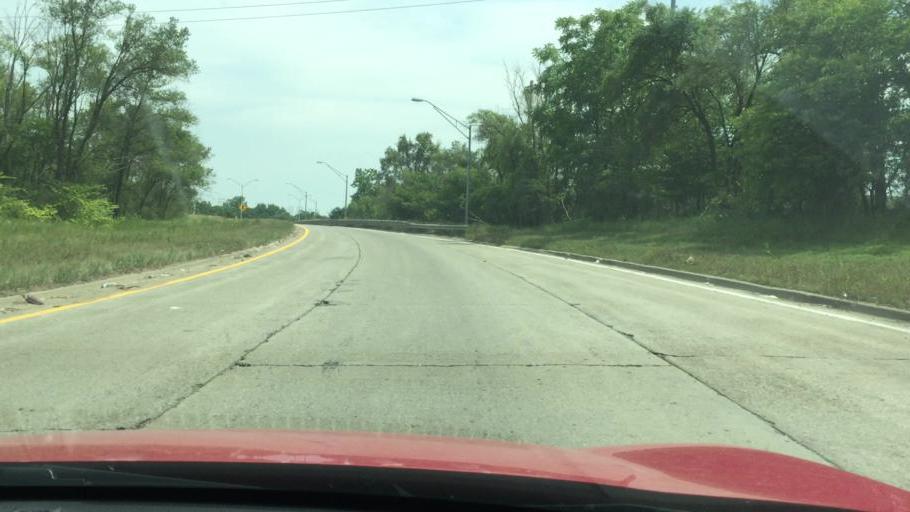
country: US
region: Michigan
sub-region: Genesee County
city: Beecher
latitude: 43.0532
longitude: -83.6746
